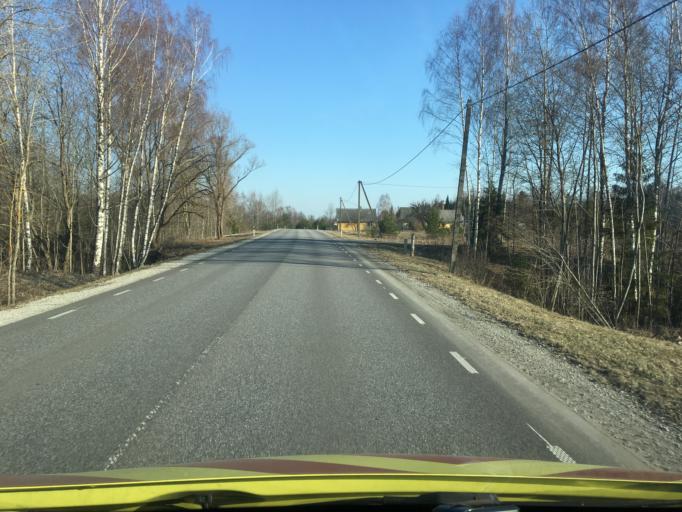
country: EE
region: Raplamaa
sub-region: Rapla vald
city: Rapla
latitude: 59.0143
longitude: 24.8373
